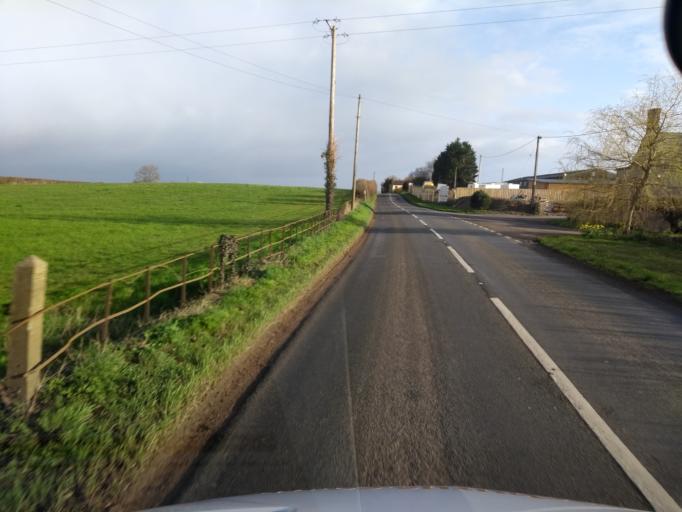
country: GB
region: England
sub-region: Somerset
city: Castle Cary
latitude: 51.0593
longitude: -2.5279
